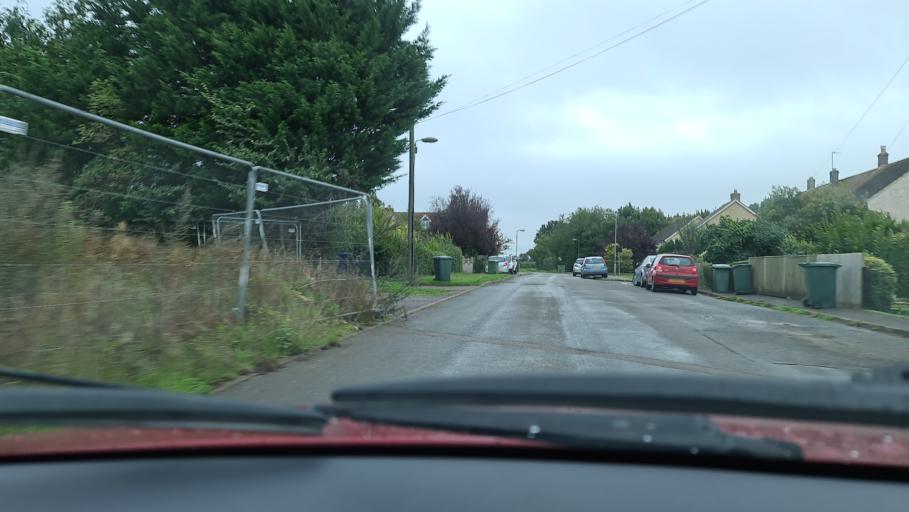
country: GB
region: England
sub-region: Oxfordshire
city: Somerton
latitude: 51.9593
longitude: -1.2319
